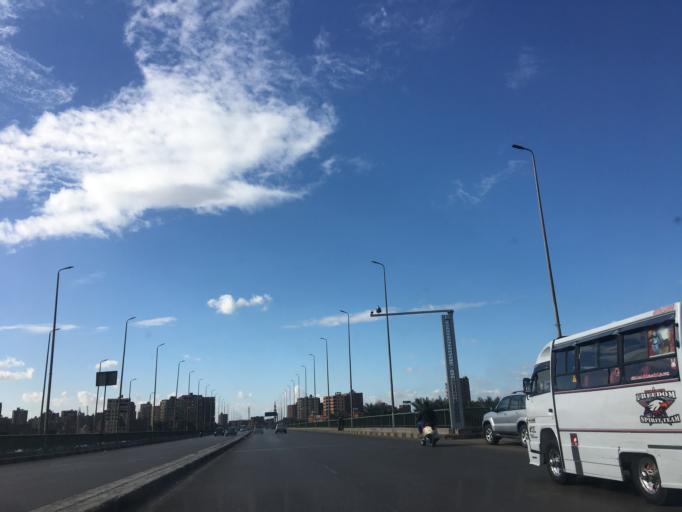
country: EG
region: Al Jizah
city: Al Jizah
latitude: 30.0286
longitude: 31.1926
